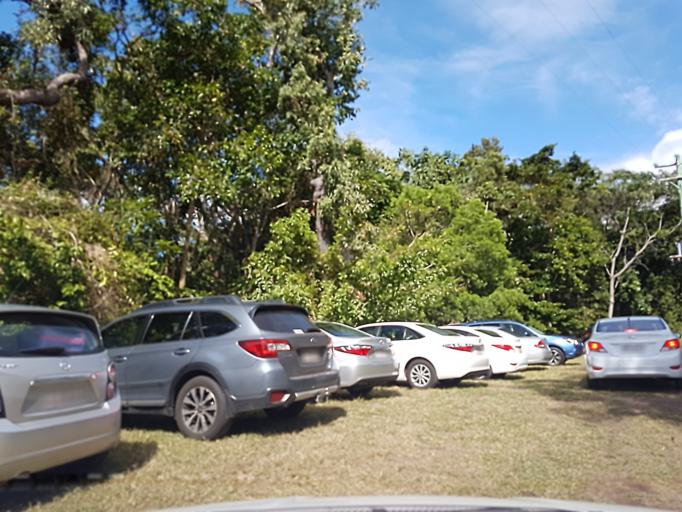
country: AU
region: Queensland
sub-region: Cairns
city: Palm Cove
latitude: -16.6624
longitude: 145.5651
